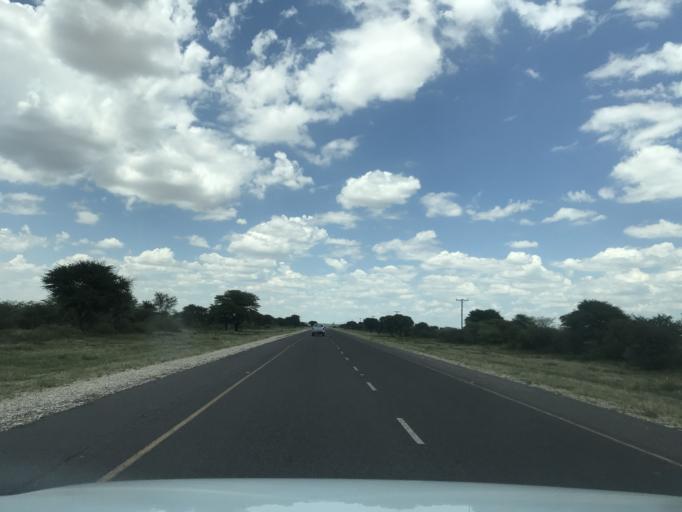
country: BW
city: Mabuli
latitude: -25.7189
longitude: 25.1167
